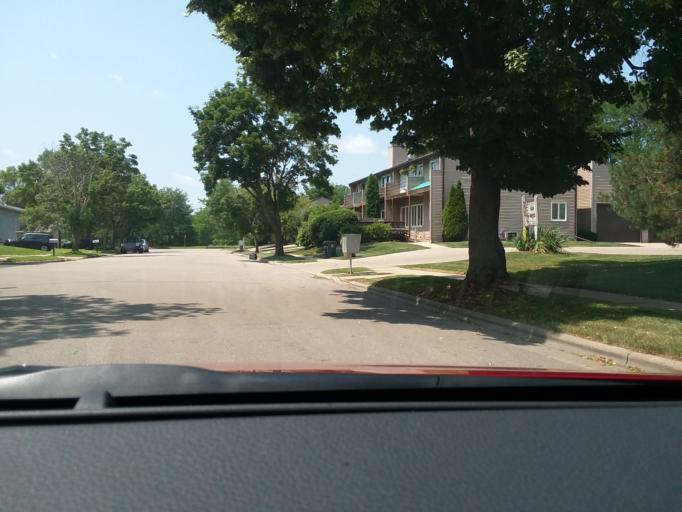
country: US
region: Wisconsin
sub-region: Dane County
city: Madison
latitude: 43.0296
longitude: -89.4175
